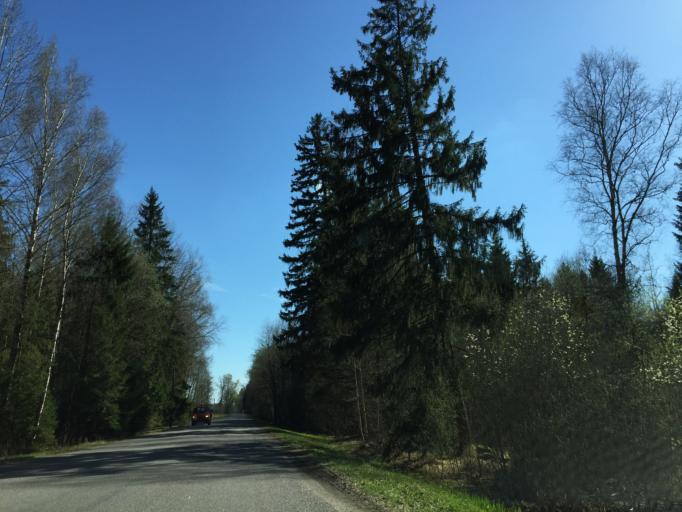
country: EE
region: Valgamaa
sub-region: Valga linn
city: Valga
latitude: 57.8629
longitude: 26.2528
